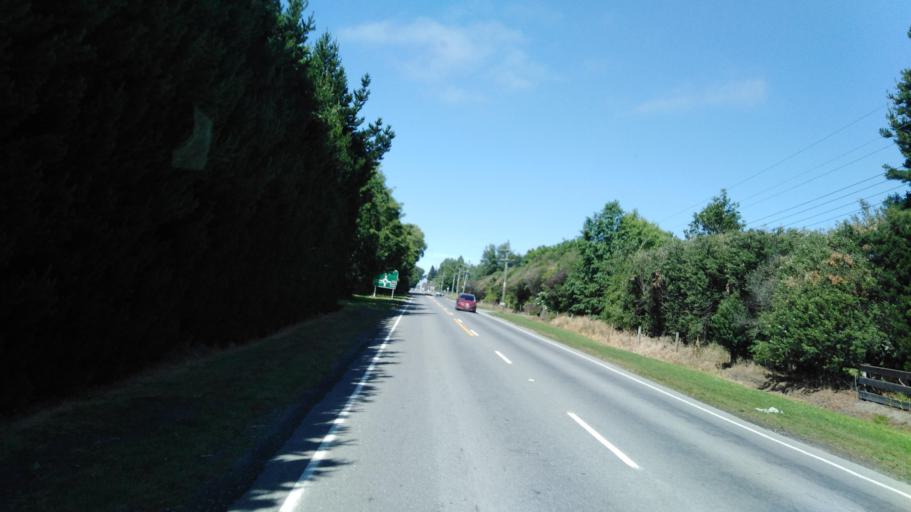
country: NZ
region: Canterbury
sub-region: Selwyn District
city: Prebbleton
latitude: -43.5174
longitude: 172.5062
